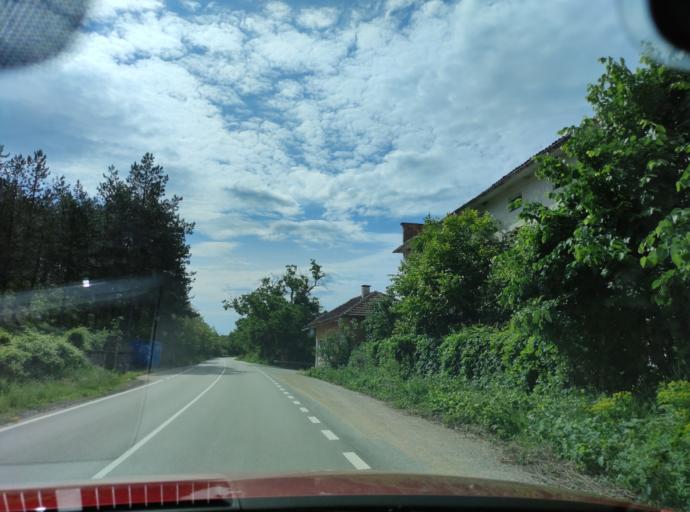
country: BG
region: Montana
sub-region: Obshtina Chiprovtsi
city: Chiprovtsi
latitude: 43.4532
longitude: 22.9054
